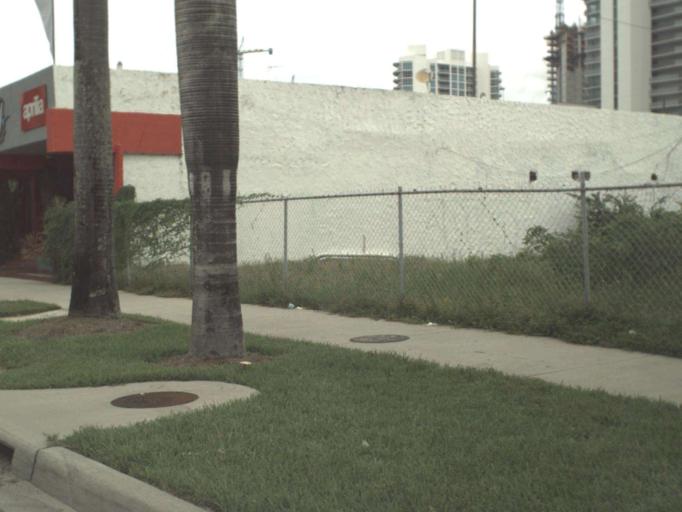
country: US
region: Florida
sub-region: Miami-Dade County
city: Miami
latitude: 25.8024
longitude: -80.1891
